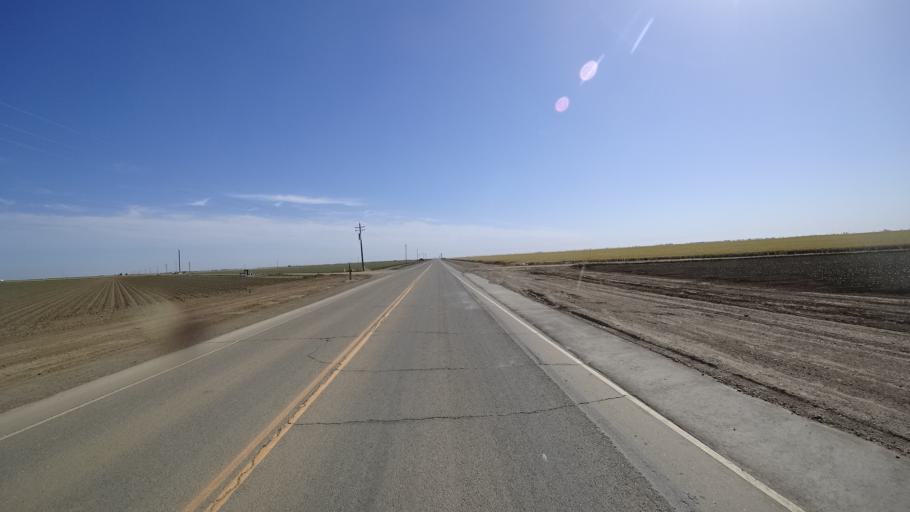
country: US
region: California
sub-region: Kings County
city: Lemoore Station
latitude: 36.1923
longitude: -119.9417
